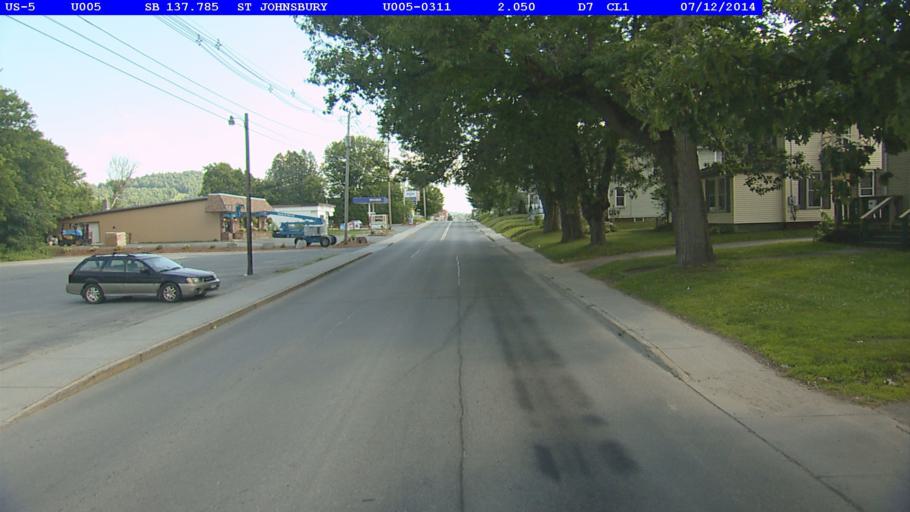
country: US
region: Vermont
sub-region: Caledonia County
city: St Johnsbury
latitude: 44.4228
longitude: -72.0148
